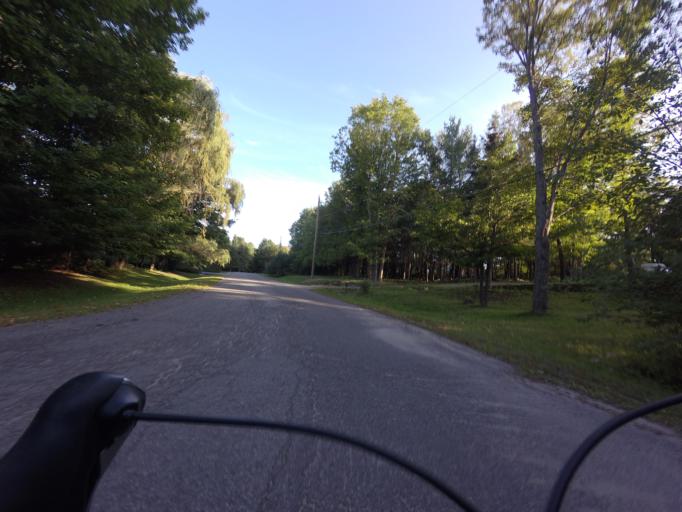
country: CA
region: Ontario
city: Bells Corners
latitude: 45.3826
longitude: -75.9652
